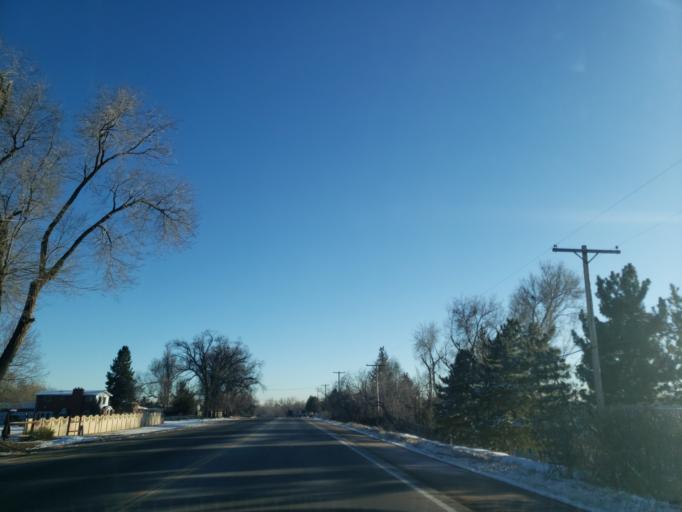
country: US
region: Colorado
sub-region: Larimer County
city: Fort Collins
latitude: 40.6361
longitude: -105.0723
